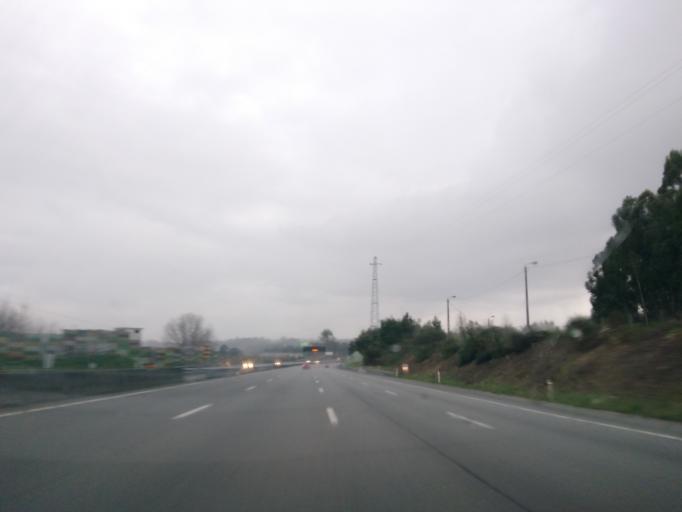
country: PT
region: Porto
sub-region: Maia
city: Aguas Santas
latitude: 41.2042
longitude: -8.5834
